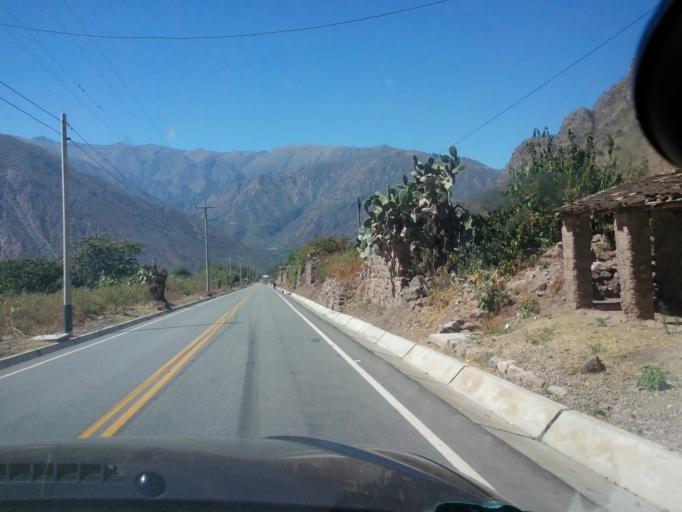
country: PE
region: Ayacucho
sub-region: Provincia de Huamanga
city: Ocros
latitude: -13.4218
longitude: -73.8577
